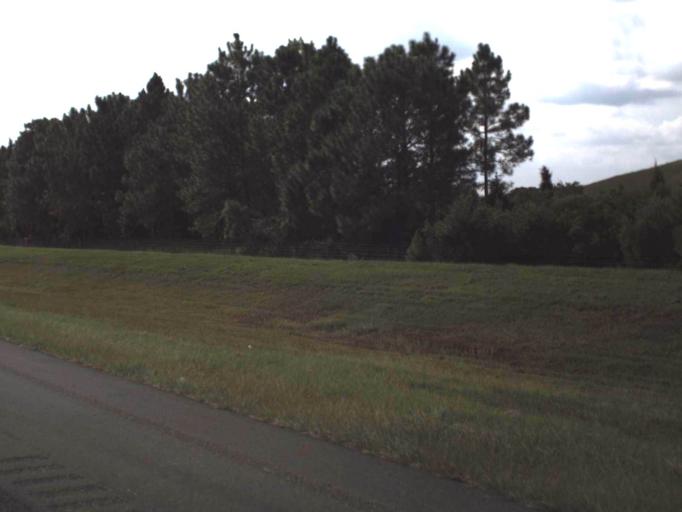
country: US
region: Florida
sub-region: Polk County
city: Fussels Corner
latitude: 28.0223
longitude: -81.8313
